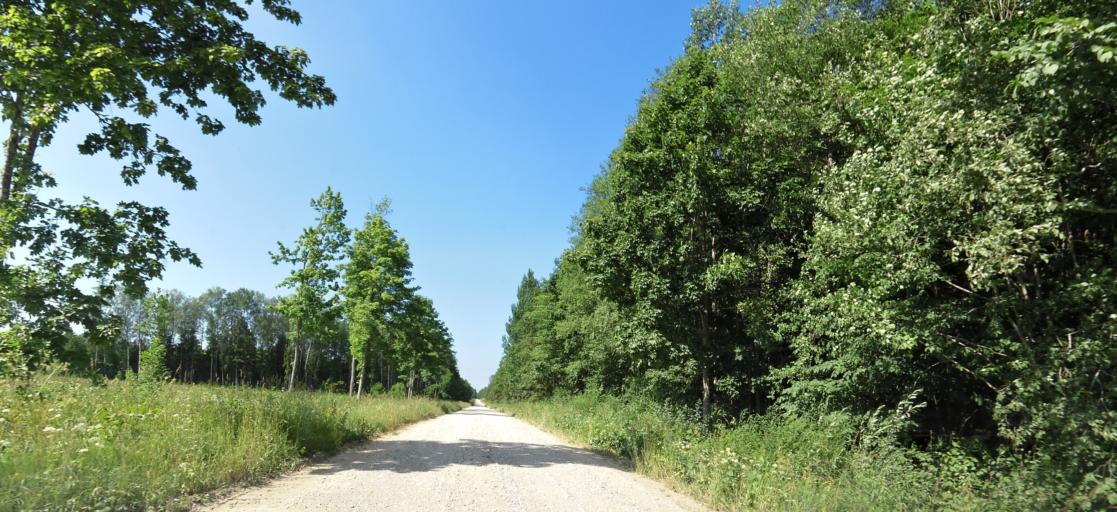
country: LT
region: Panevezys
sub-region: Birzai
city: Birzai
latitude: 56.2197
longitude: 24.9387
